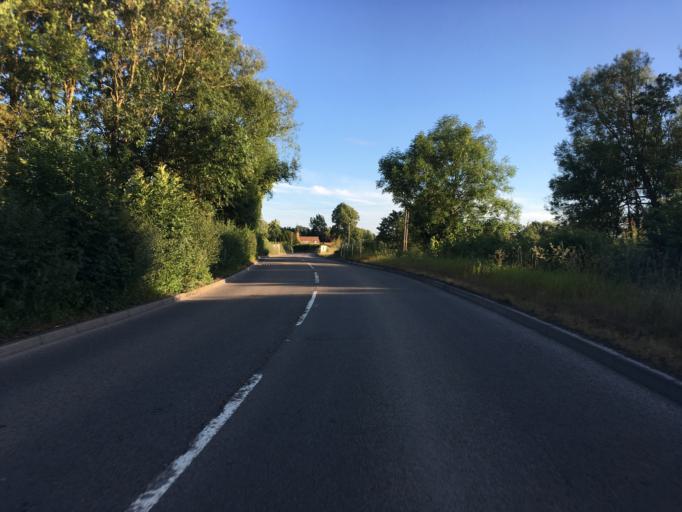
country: GB
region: England
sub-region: Hampshire
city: Tadley
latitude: 51.3891
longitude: -1.1542
